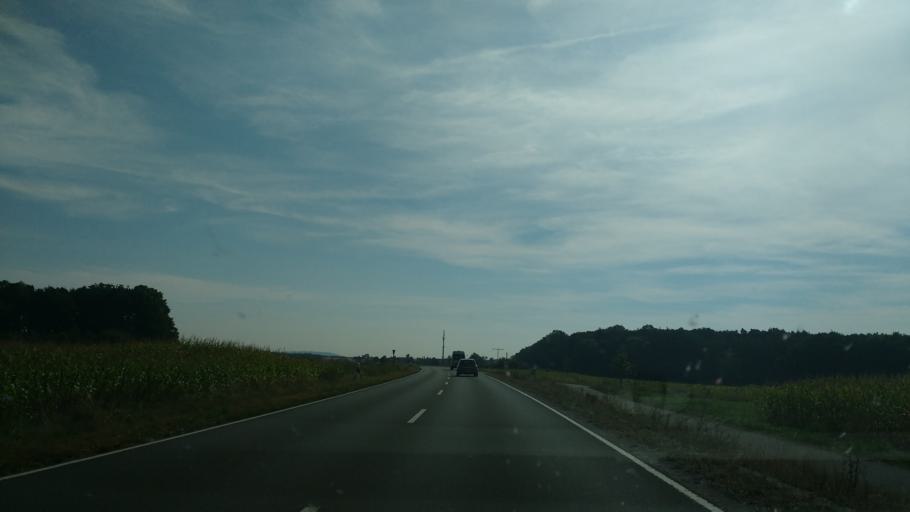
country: DE
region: Bavaria
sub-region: Regierungsbezirk Mittelfranken
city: Grossenseebach
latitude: 49.6320
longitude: 10.8892
